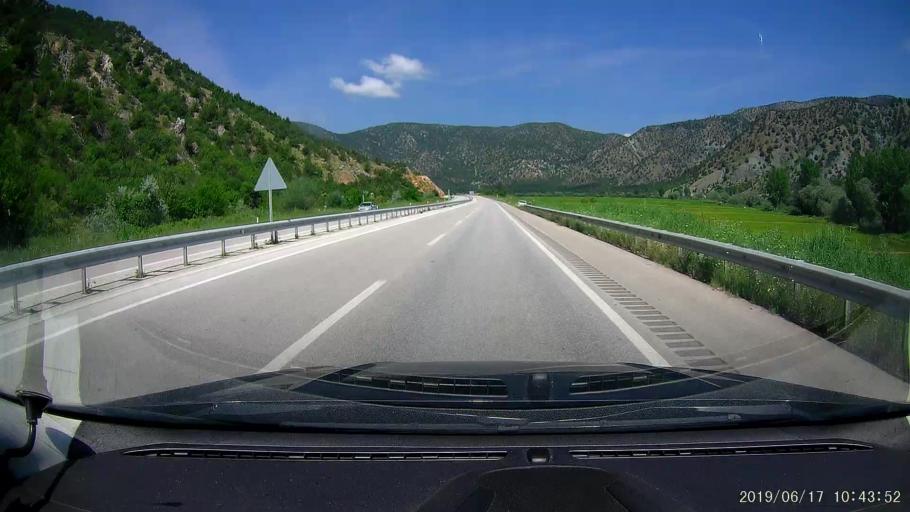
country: TR
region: Corum
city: Kargi
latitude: 41.0696
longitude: 34.5260
